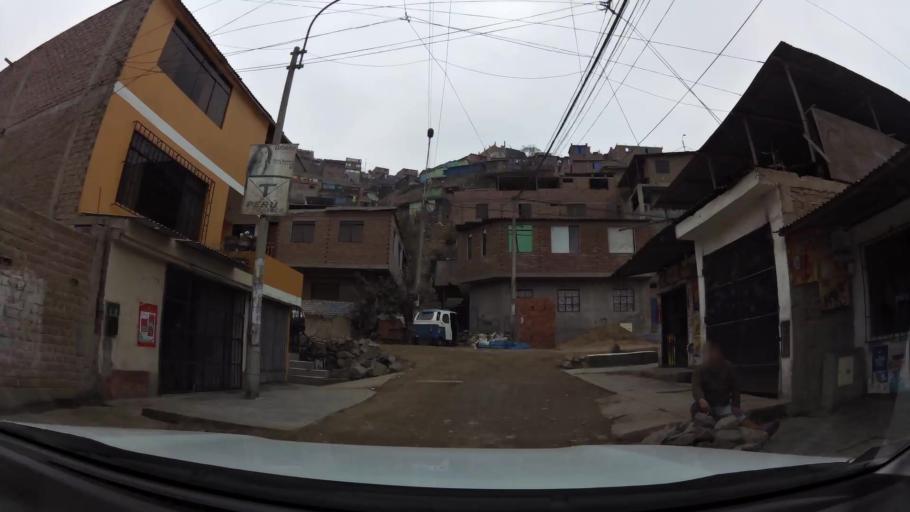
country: PE
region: Lima
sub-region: Lima
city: Surco
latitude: -12.1761
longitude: -76.9522
